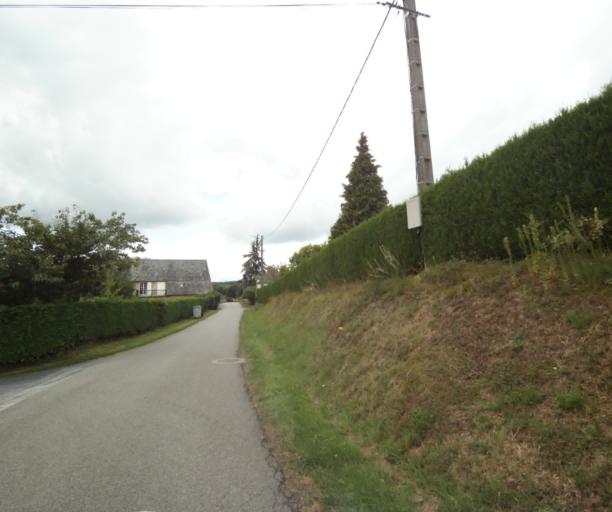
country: FR
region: Limousin
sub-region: Departement de la Correze
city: Sainte-Fortunade
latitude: 45.1834
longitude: 1.8132
